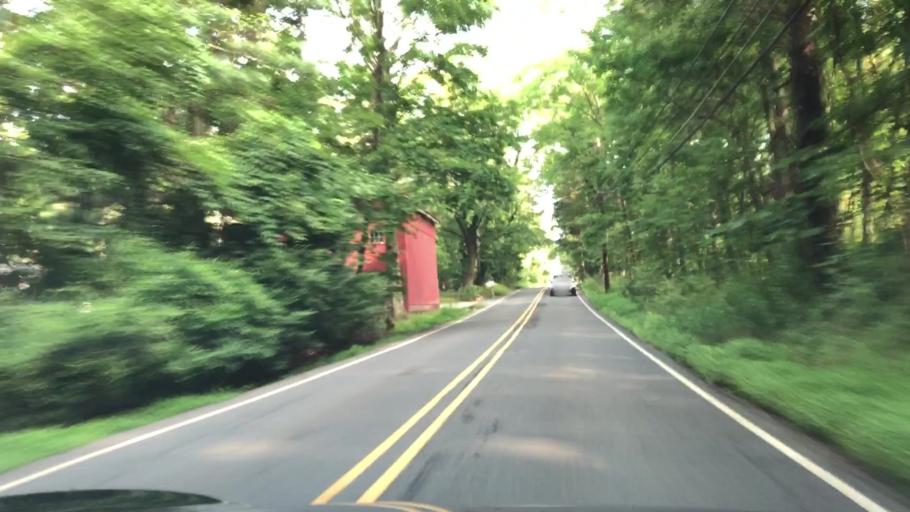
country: US
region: New Jersey
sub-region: Mercer County
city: Princeton
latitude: 40.3403
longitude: -74.7033
